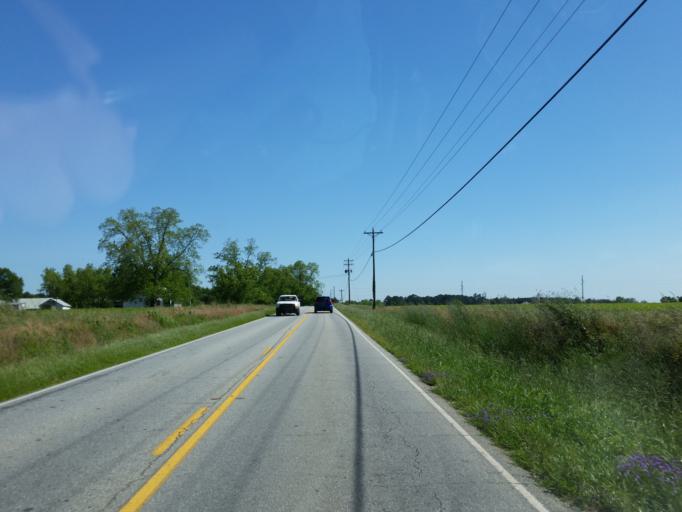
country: US
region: Georgia
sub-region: Lowndes County
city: Hahira
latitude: 30.9382
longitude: -83.3497
